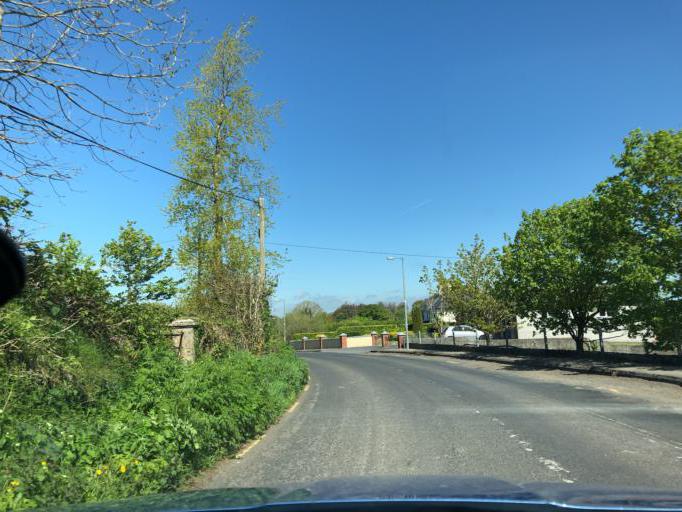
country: IE
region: Connaught
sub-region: County Galway
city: Portumna
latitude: 53.1413
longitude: -8.3672
